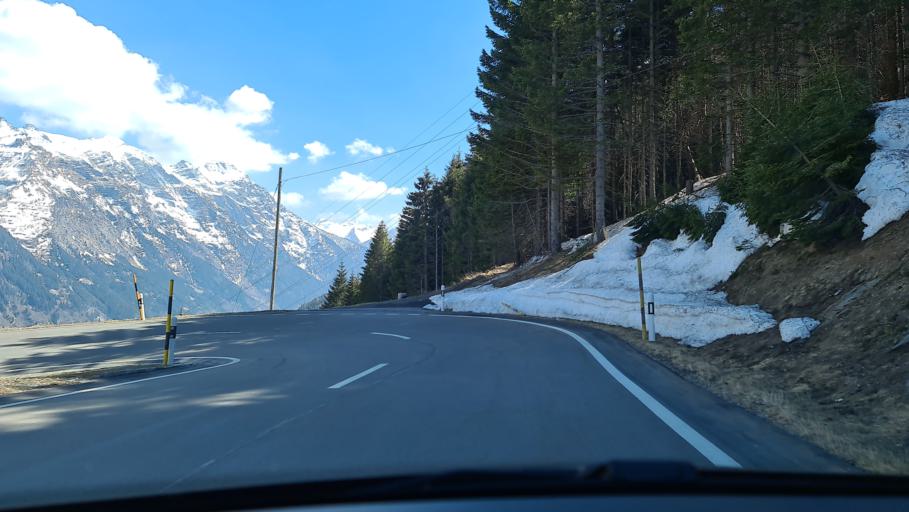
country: CH
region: Grisons
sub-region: Moesa District
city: Mesocco
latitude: 46.4350
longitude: 9.2041
